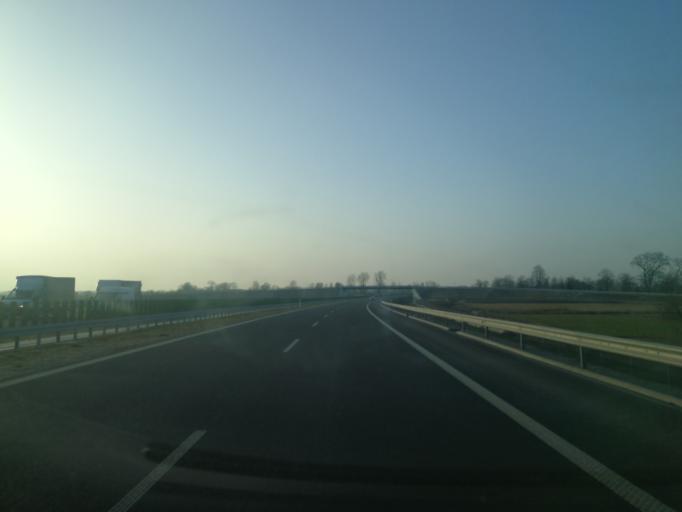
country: PL
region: Pomeranian Voivodeship
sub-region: Powiat nowodworski
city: Nowy Dwor Gdanski
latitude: 54.1748
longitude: 19.1946
